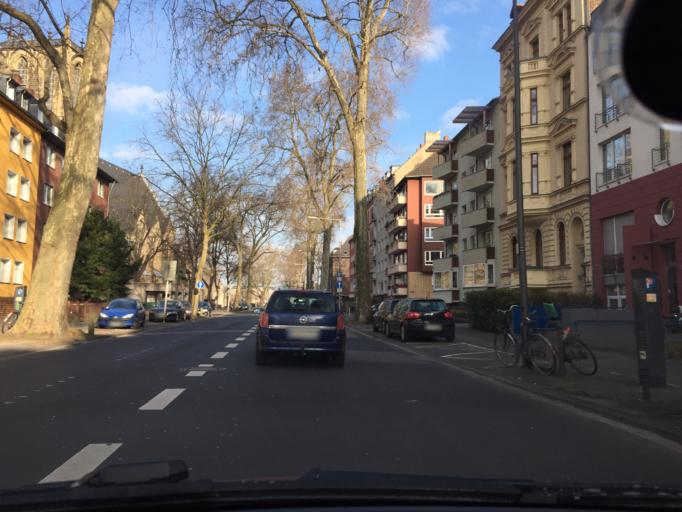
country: DE
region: North Rhine-Westphalia
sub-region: Regierungsbezirk Koln
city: Neustadt/Sued
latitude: 50.9215
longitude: 6.9514
